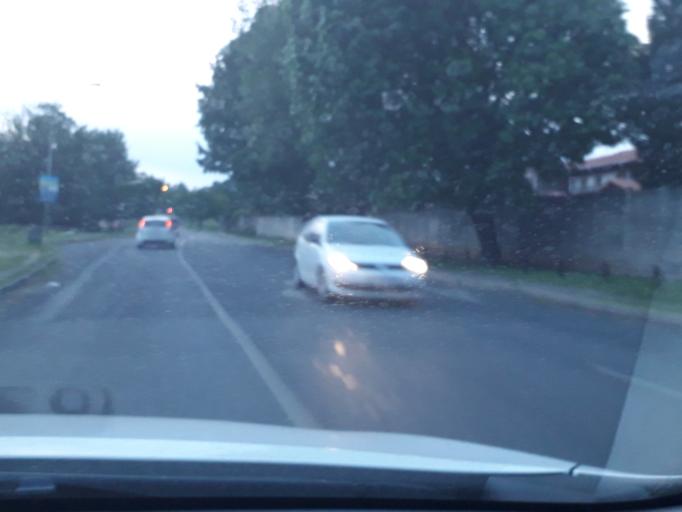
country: ZA
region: Gauteng
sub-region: City of Johannesburg Metropolitan Municipality
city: Johannesburg
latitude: -26.1447
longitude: 28.0031
